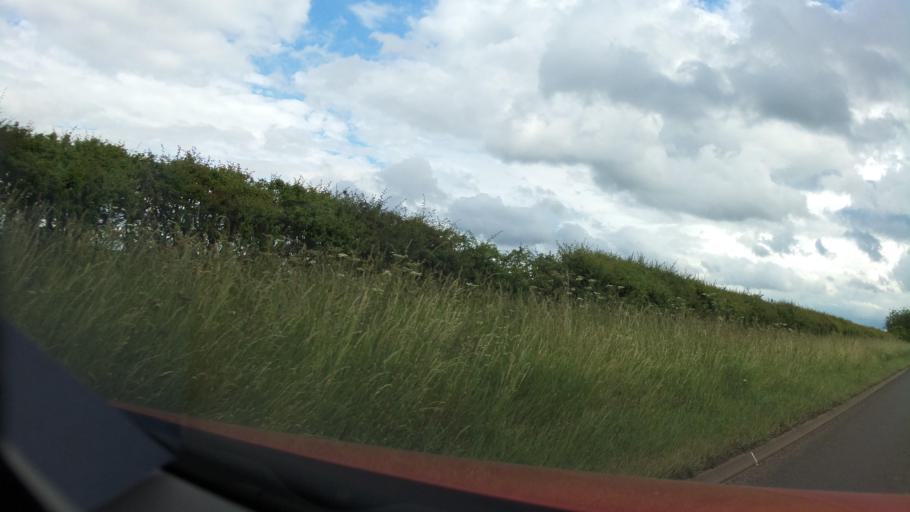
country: GB
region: England
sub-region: Worcestershire
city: Kidderminster
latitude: 52.4395
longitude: -2.2116
